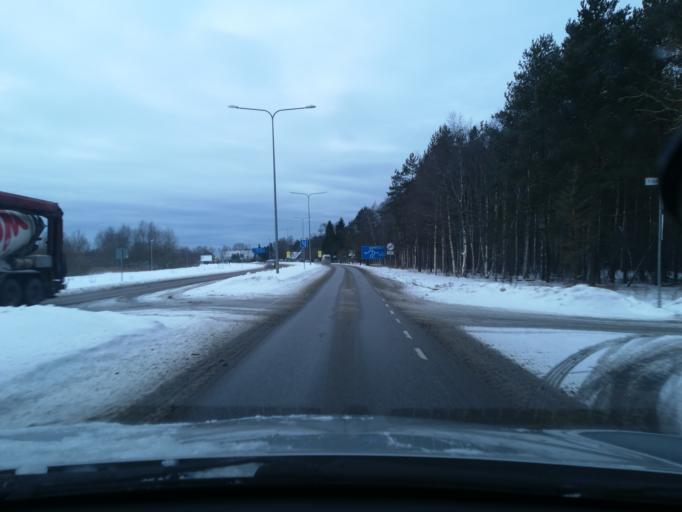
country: EE
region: Harju
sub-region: Harku vald
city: Tabasalu
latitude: 59.4363
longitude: 24.5801
